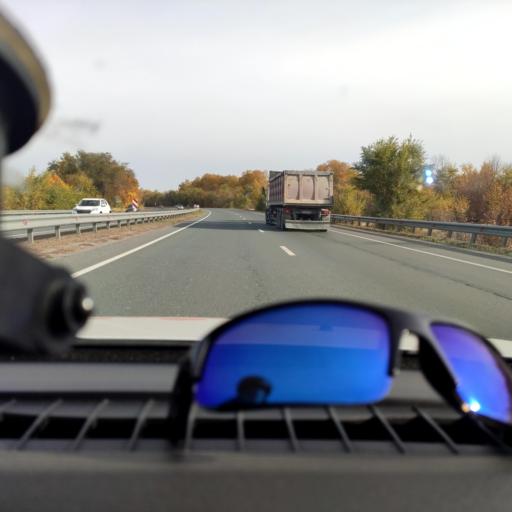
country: RU
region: Samara
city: Novokuybyshevsk
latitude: 53.0272
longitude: 49.9912
